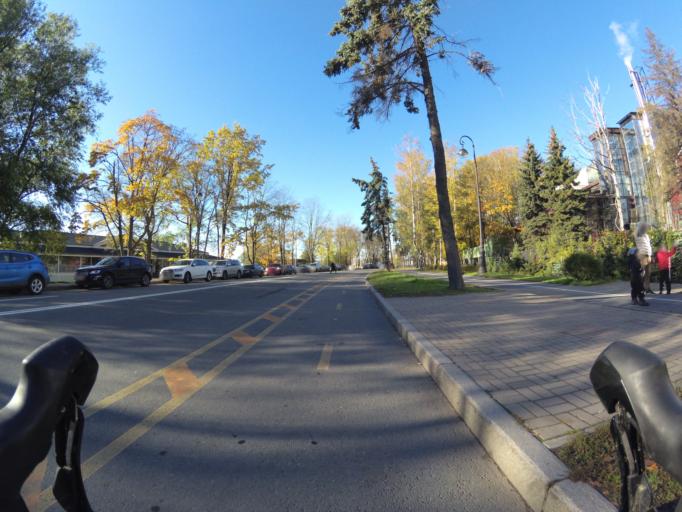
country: RU
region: Leningrad
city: Krestovskiy ostrov
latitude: 59.9686
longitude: 30.2378
